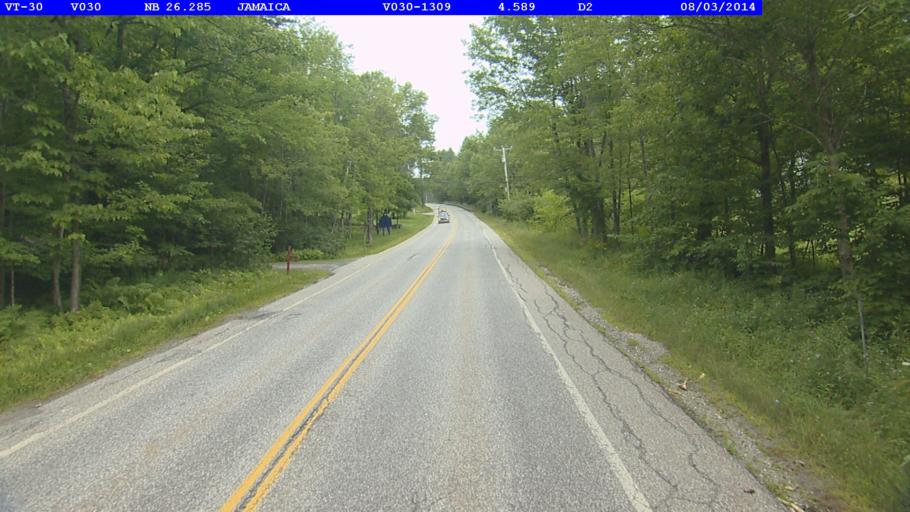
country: US
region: Vermont
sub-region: Windham County
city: Dover
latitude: 43.1016
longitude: -72.7910
